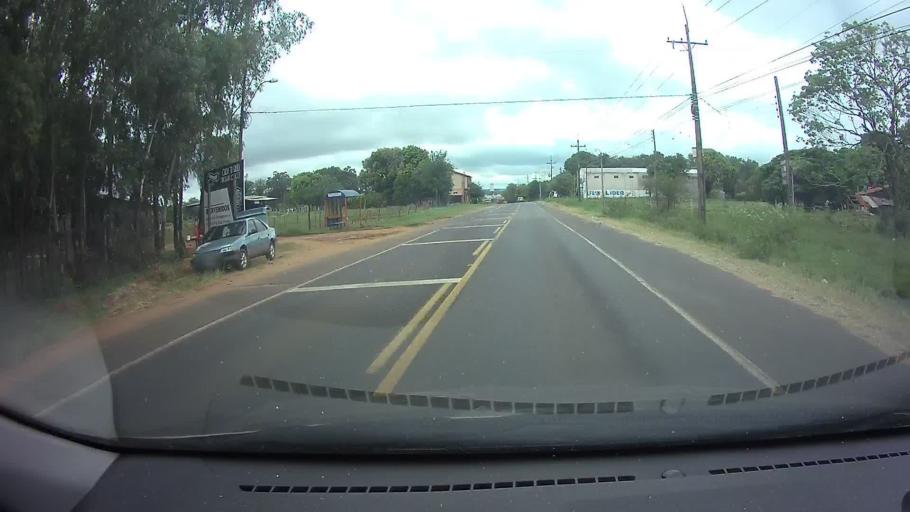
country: PY
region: Central
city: Guarambare
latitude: -25.5005
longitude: -57.4890
